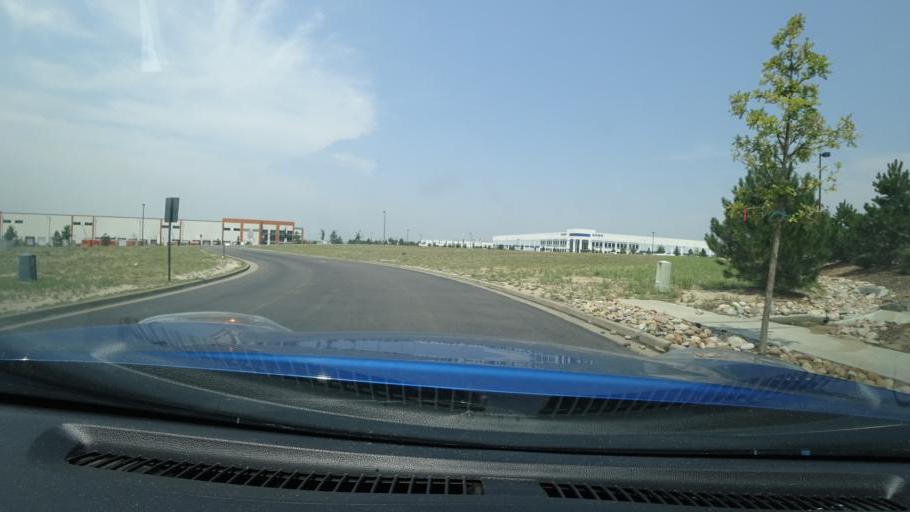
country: US
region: Colorado
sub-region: Adams County
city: Aurora
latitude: 39.7679
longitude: -104.7734
